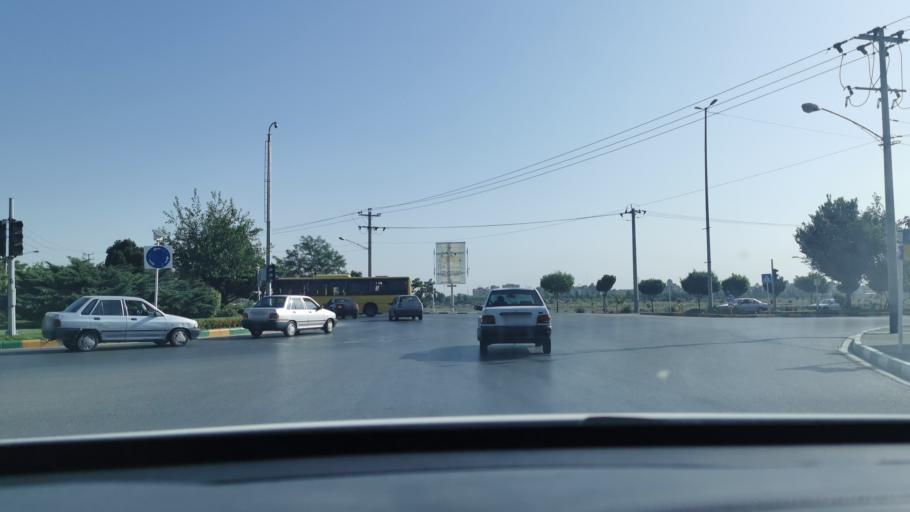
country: IR
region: Razavi Khorasan
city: Mashhad
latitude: 36.3408
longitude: 59.5078
